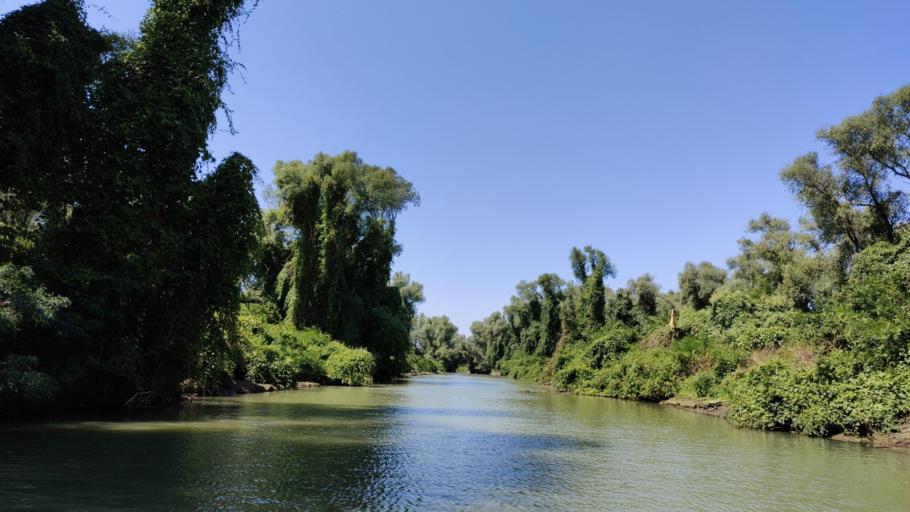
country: RO
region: Tulcea
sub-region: Comuna Pardina
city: Pardina
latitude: 45.2550
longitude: 28.9435
